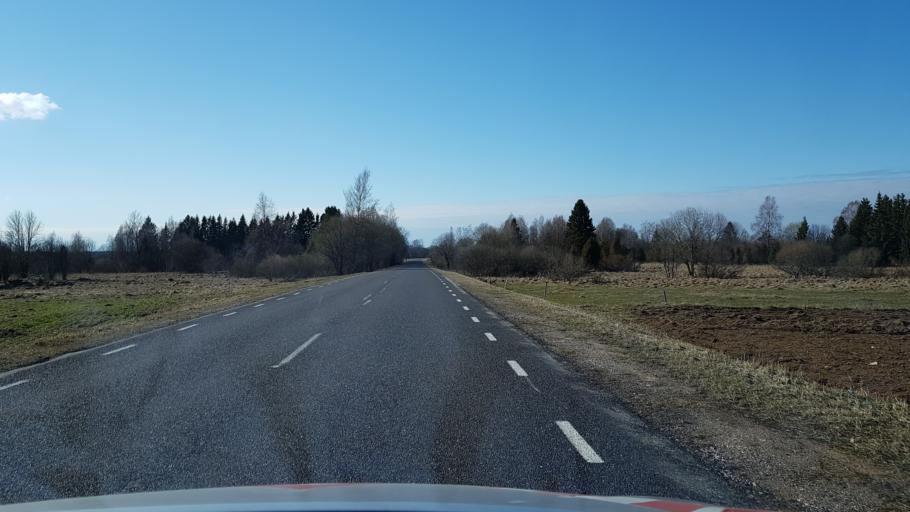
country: EE
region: Laeaene-Virumaa
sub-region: Kadrina vald
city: Kadrina
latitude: 59.5306
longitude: 26.0629
